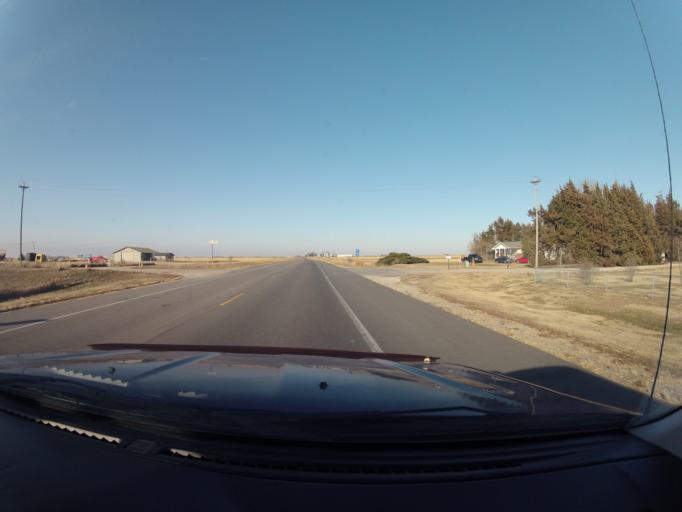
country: US
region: Nebraska
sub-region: Kearney County
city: Minden
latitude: 40.5172
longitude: -98.9518
